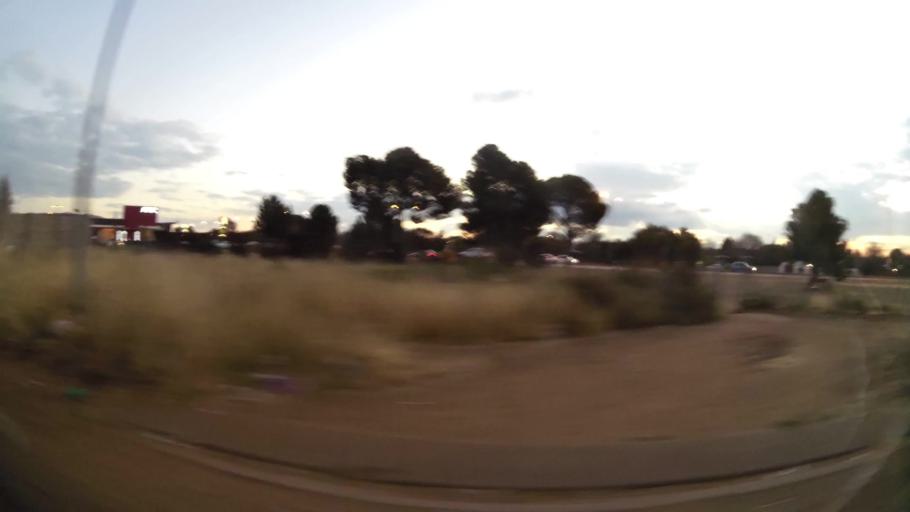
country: ZA
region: Orange Free State
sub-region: Mangaung Metropolitan Municipality
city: Bloemfontein
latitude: -29.1530
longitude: 26.1900
